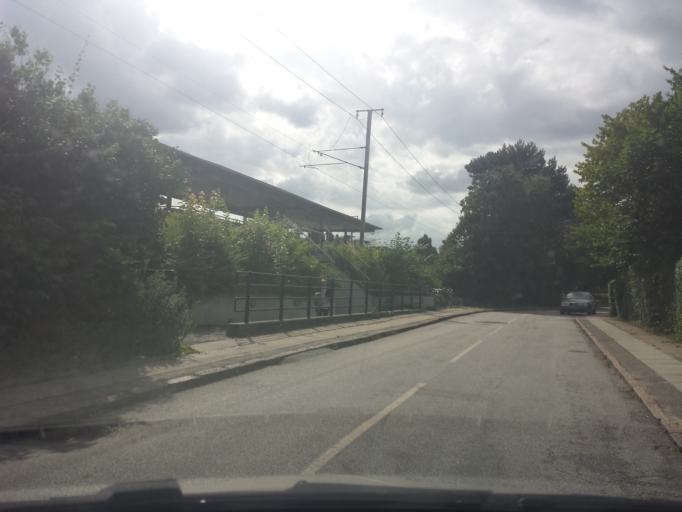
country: DK
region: Capital Region
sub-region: Herlev Kommune
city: Herlev
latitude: 55.7231
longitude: 12.4038
